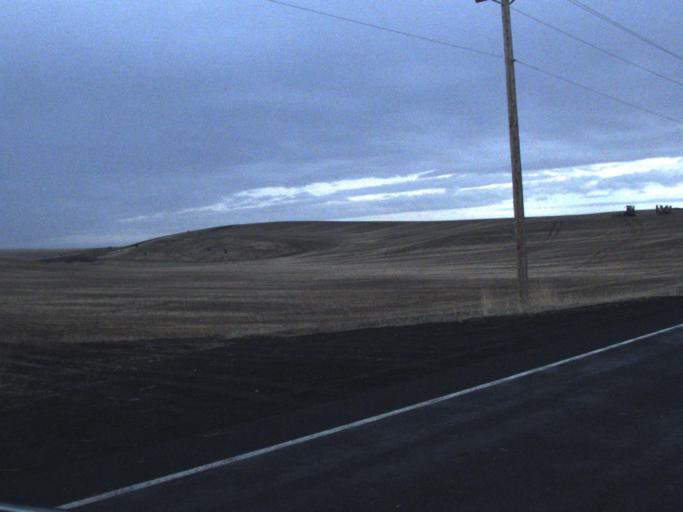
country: US
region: Washington
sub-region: Lincoln County
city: Davenport
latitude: 47.7708
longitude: -118.1735
